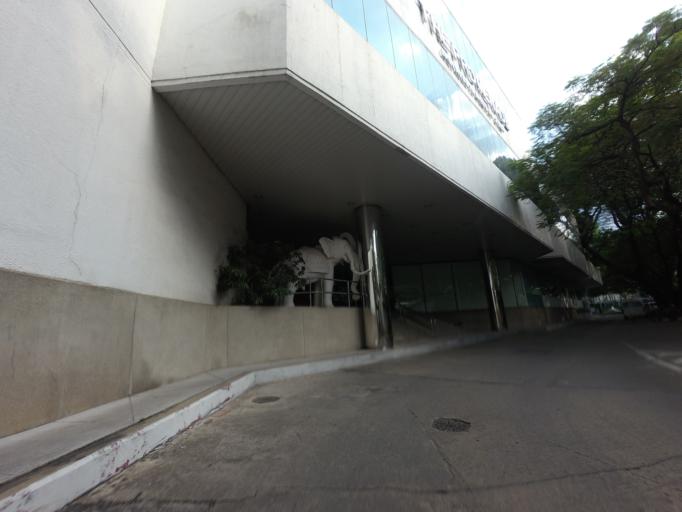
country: TH
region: Bangkok
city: Ratchathewi
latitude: 13.7478
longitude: 100.5473
